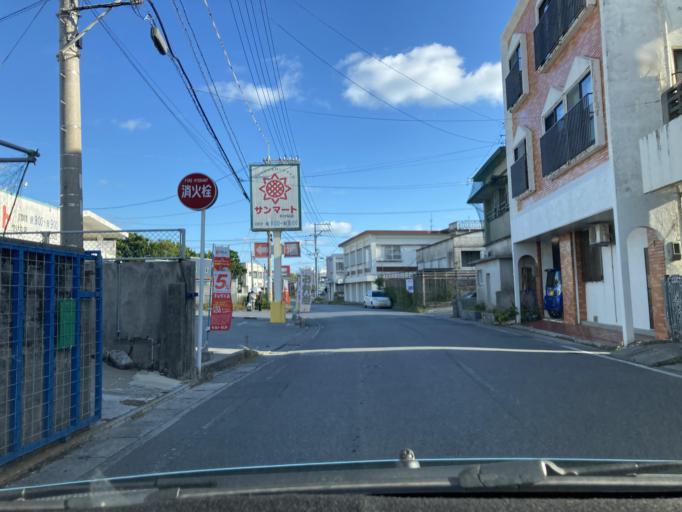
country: JP
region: Okinawa
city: Katsuren-haebaru
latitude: 26.3247
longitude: 127.9054
